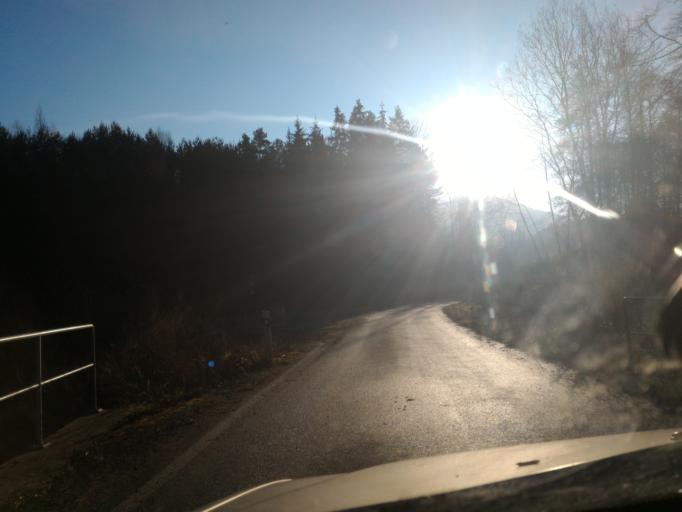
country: DE
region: Saxony
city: Kurort Oybin
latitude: 50.8070
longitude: 14.7188
